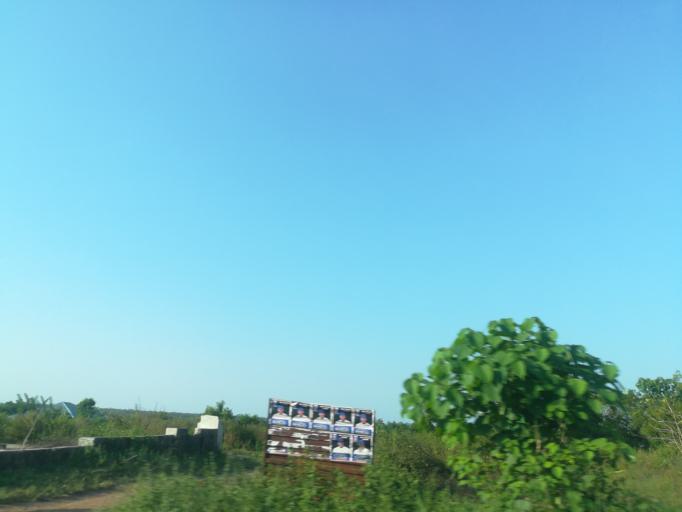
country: NG
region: Ogun
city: Abeokuta
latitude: 7.1842
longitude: 3.2738
